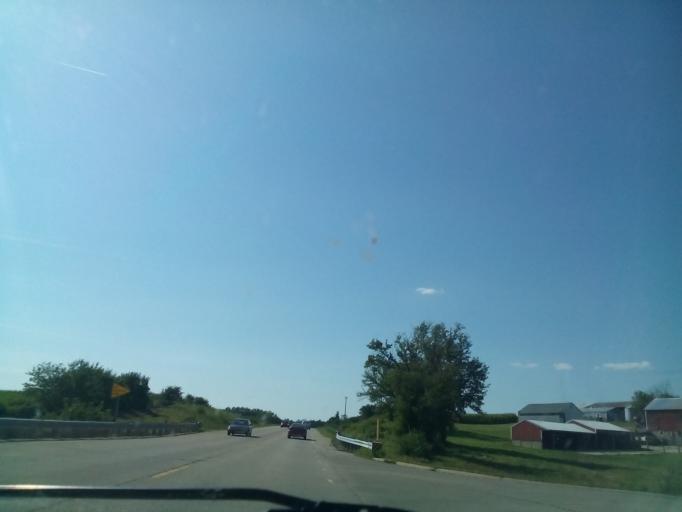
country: US
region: Wisconsin
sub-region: Dane County
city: Belleville
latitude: 42.8638
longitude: -89.5920
